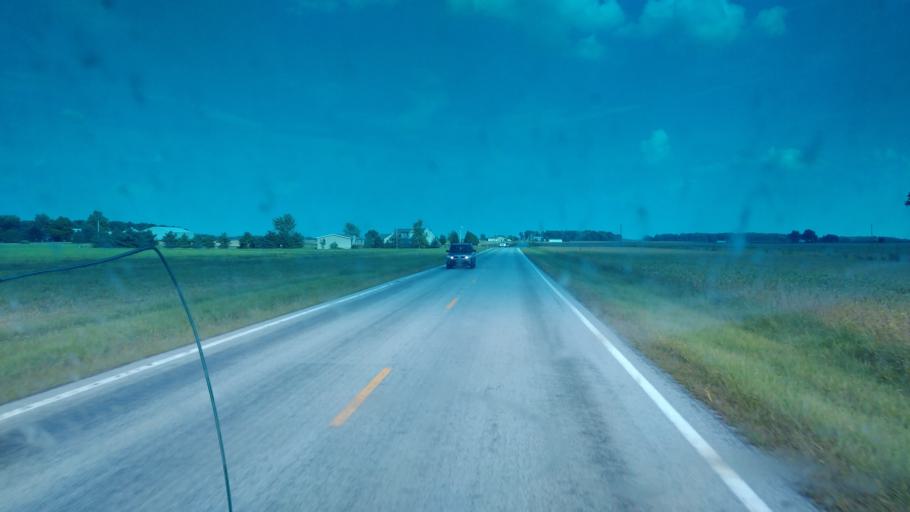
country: US
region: Ohio
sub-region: Hardin County
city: Forest
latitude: 40.8910
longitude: -83.5414
